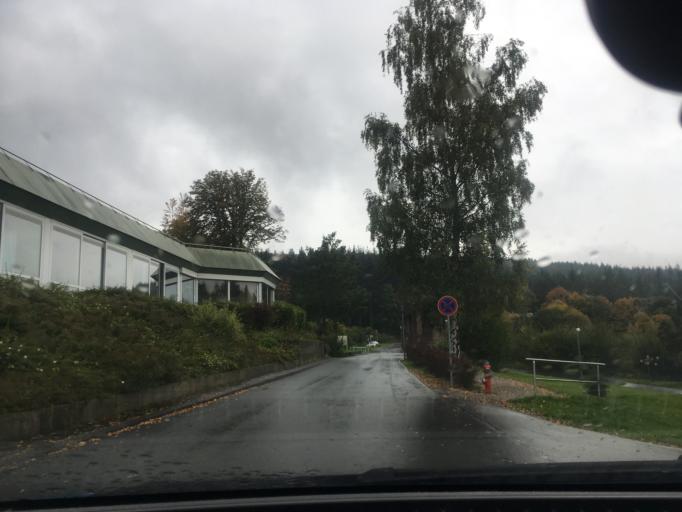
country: DE
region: Lower Saxony
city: Bodenfelde
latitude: 51.6150
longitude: 9.5898
